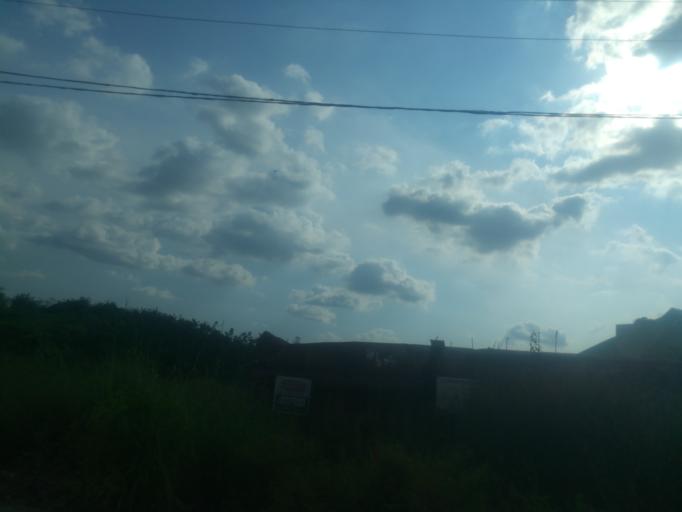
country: NG
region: Oyo
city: Ibadan
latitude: 7.4159
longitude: 3.8515
